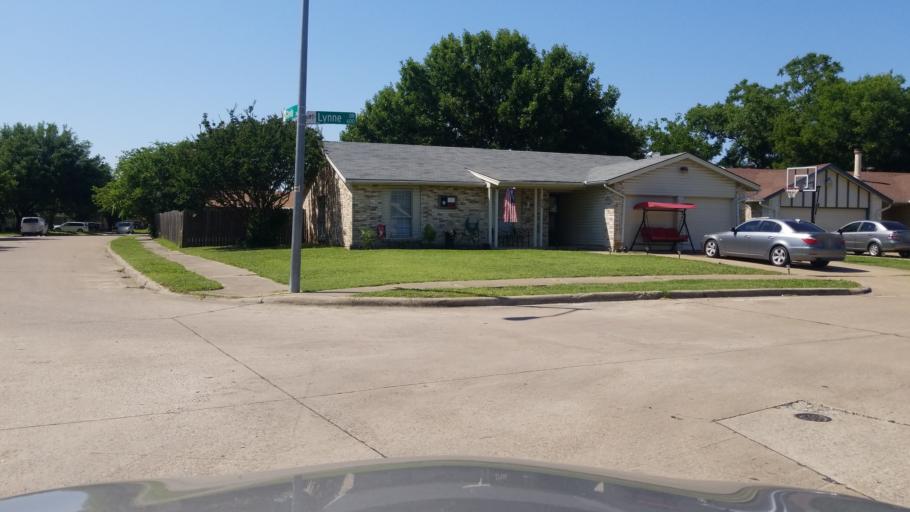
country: US
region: Texas
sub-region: Dallas County
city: Grand Prairie
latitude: 32.6865
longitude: -97.0126
